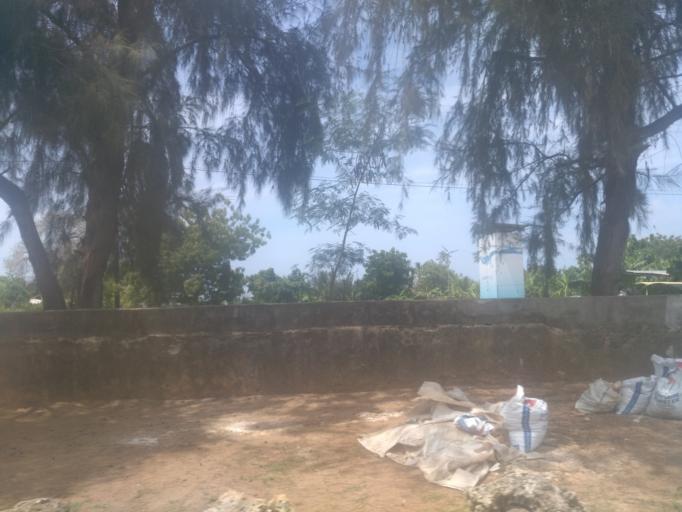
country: TZ
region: Zanzibar Urban/West
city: Zanzibar
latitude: -6.2192
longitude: 39.2130
